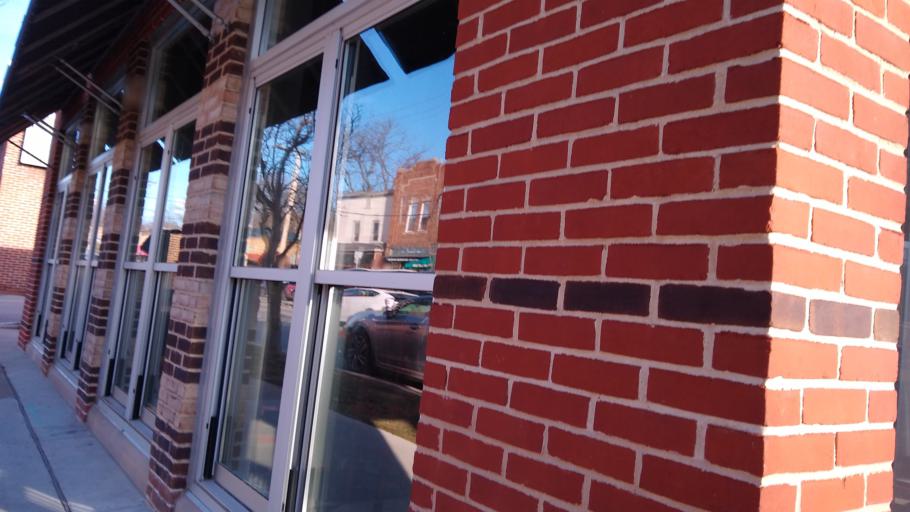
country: US
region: Wisconsin
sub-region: Dane County
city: Shorewood Hills
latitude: 43.0574
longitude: -89.4285
